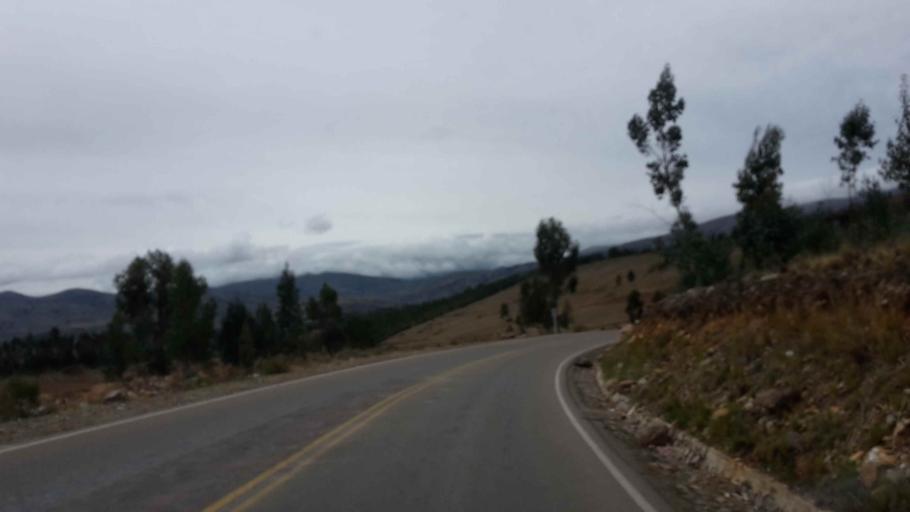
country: BO
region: Cochabamba
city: Arani
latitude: -17.4650
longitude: -65.6973
